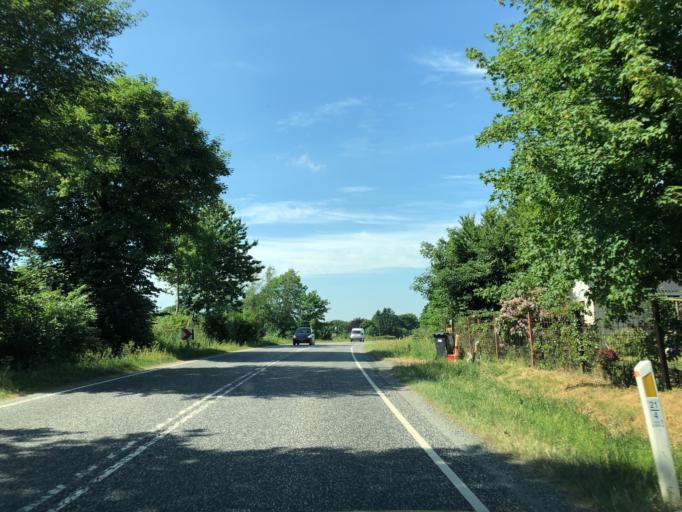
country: DK
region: South Denmark
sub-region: Vejle Kommune
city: Give
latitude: 55.7723
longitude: 9.2849
